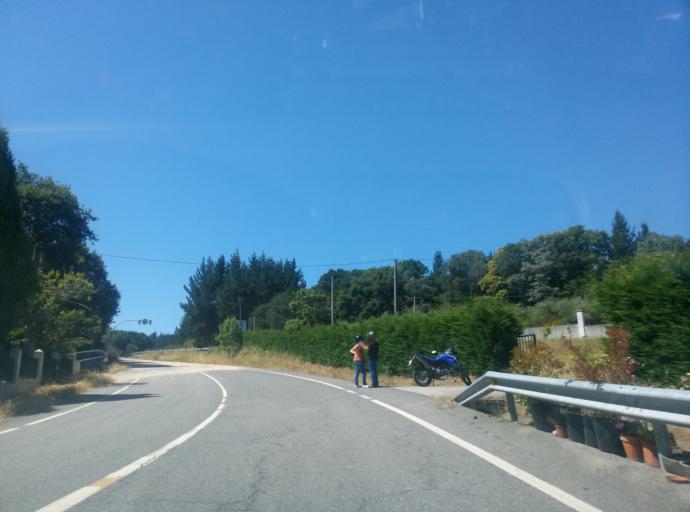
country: ES
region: Galicia
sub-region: Provincia de Lugo
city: Mos
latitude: 43.0980
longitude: -7.4777
